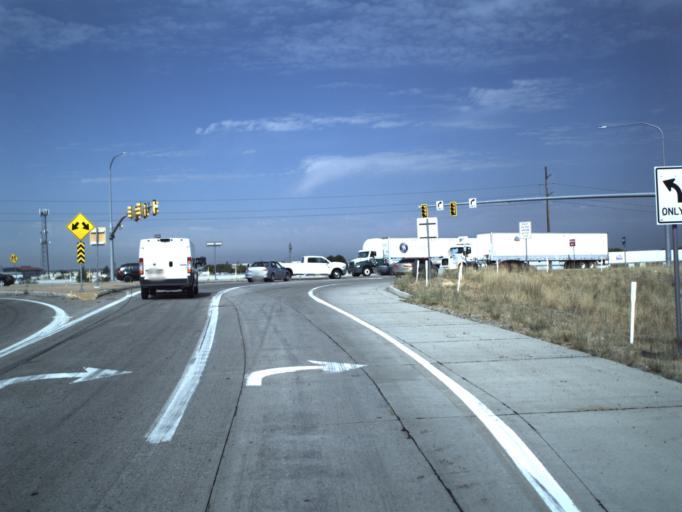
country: US
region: Utah
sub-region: Salt Lake County
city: West Valley City
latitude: 40.7269
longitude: -111.9855
